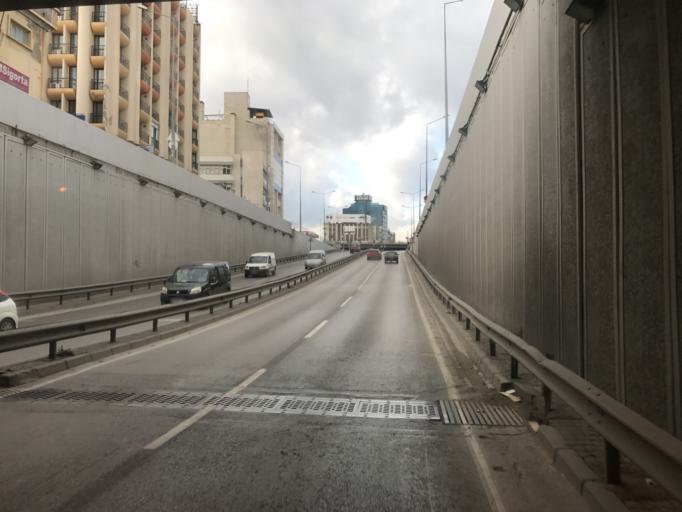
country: TR
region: Izmir
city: Izmir
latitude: 38.4227
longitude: 27.1555
